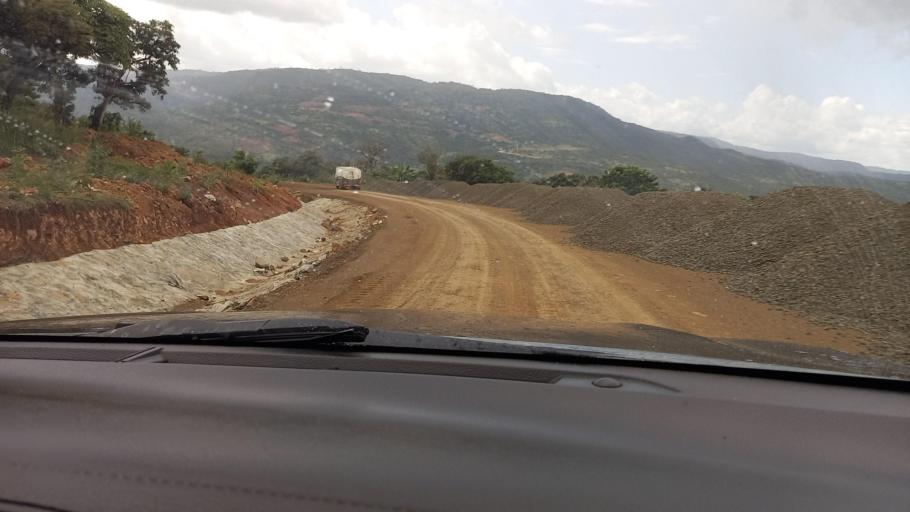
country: ET
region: Southern Nations, Nationalities, and People's Region
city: Mizan Teferi
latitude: 6.1864
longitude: 35.6910
